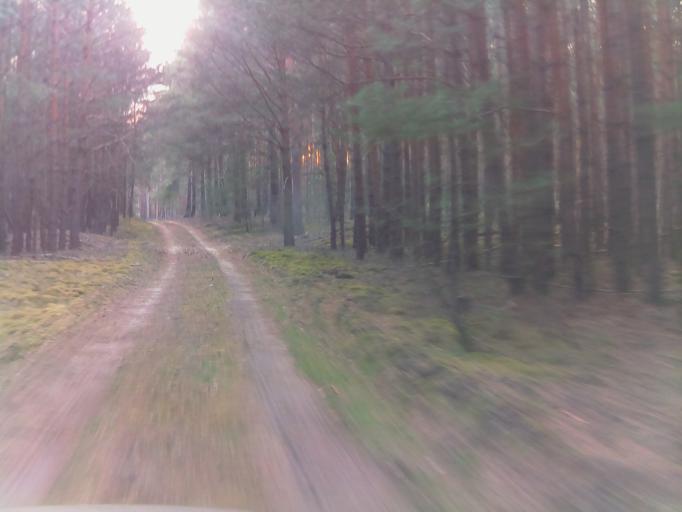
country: DE
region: Brandenburg
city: Jamlitz
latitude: 51.9687
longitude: 14.4264
